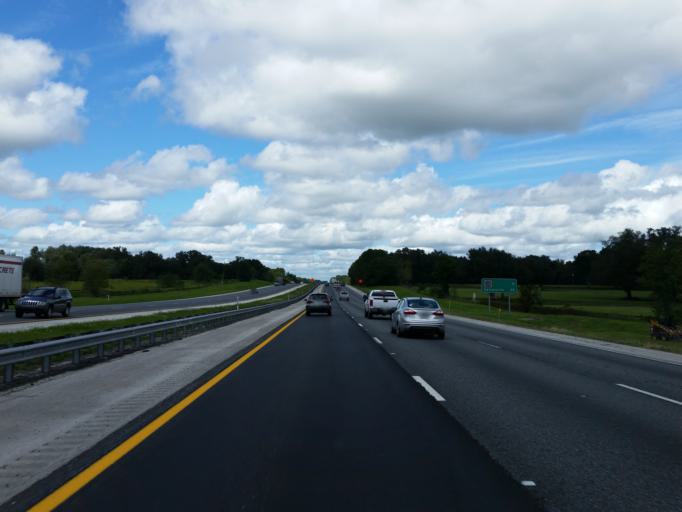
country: US
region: Florida
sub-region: Marion County
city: Ocala
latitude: 29.2812
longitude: -82.1982
